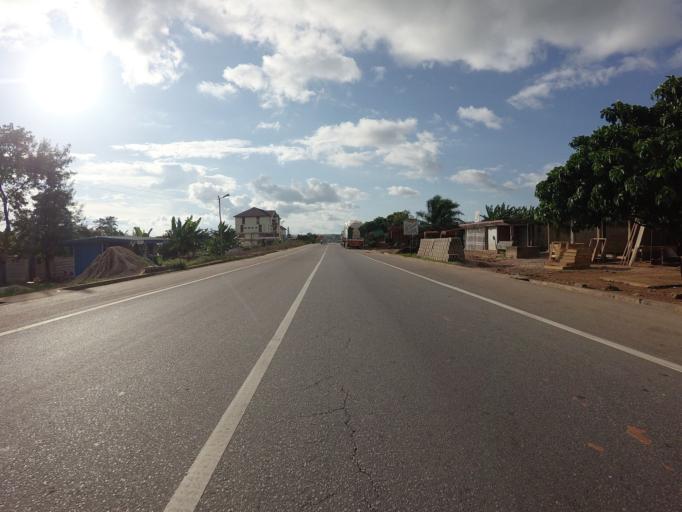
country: GH
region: Ashanti
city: Tafo
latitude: 6.8794
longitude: -1.6421
